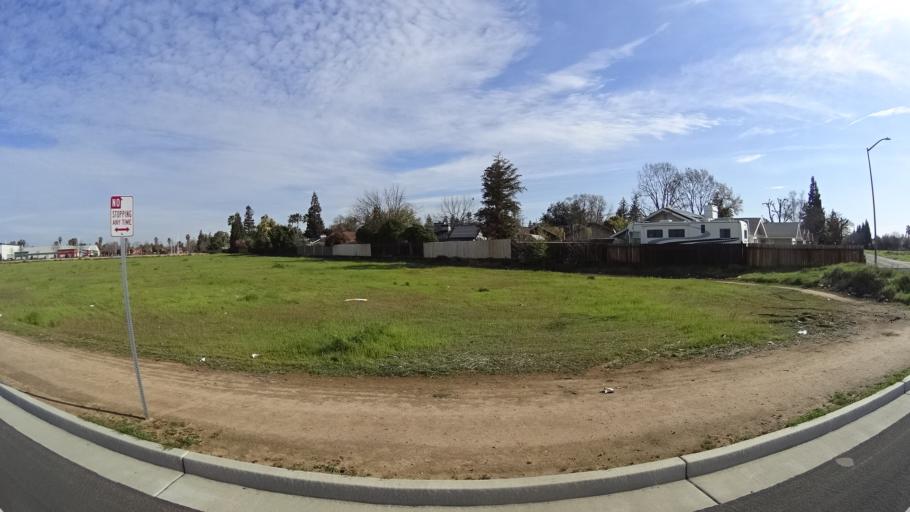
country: US
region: California
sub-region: Fresno County
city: West Park
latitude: 36.8301
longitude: -119.8740
